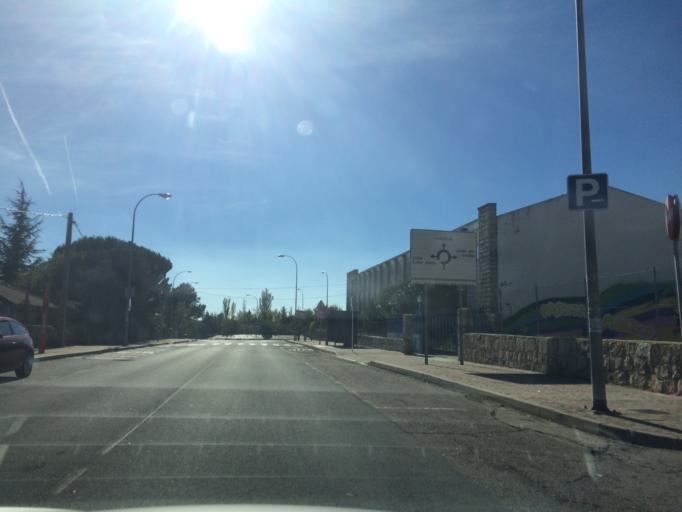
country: ES
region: Madrid
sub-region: Provincia de Madrid
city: La Cabrera
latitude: 40.8626
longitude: -3.6134
